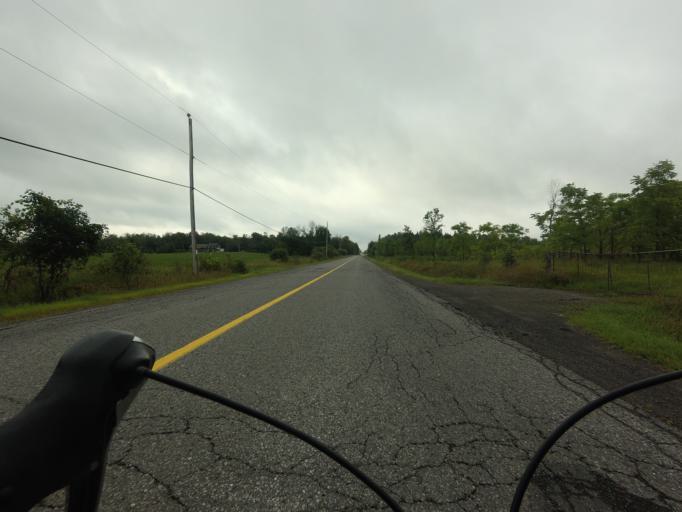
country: CA
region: Ontario
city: Bells Corners
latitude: 45.1043
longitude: -75.7722
